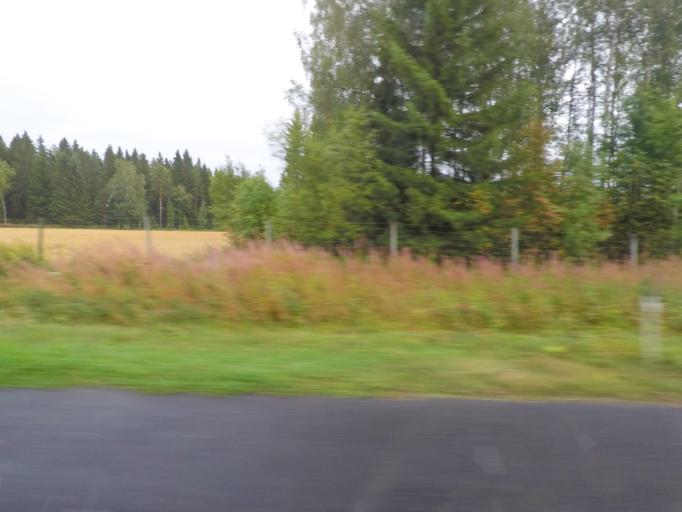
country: FI
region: Southern Savonia
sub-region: Pieksaemaeki
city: Joroinen
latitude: 62.2153
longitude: 27.8775
